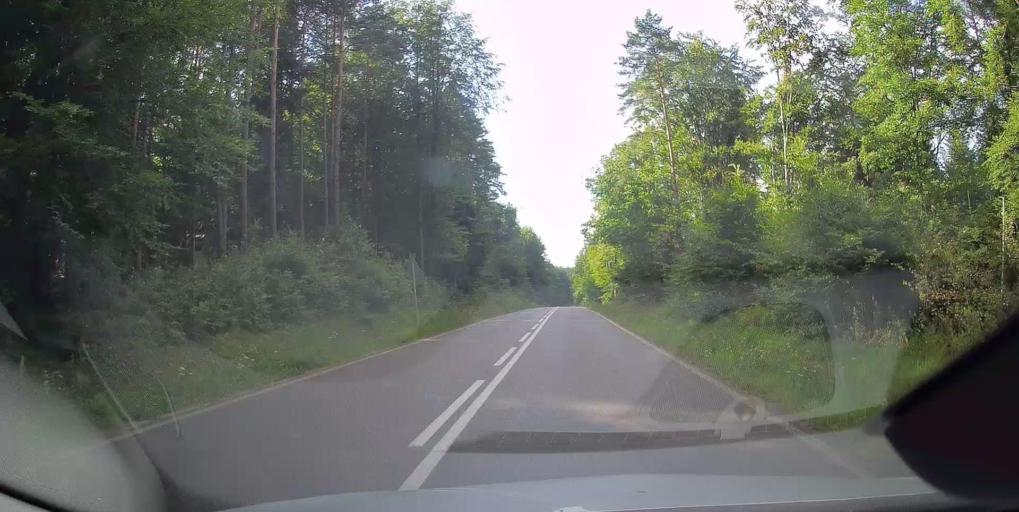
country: PL
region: Swietokrzyskie
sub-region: Powiat skarzyski
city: Suchedniow
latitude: 50.9937
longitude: 20.8578
